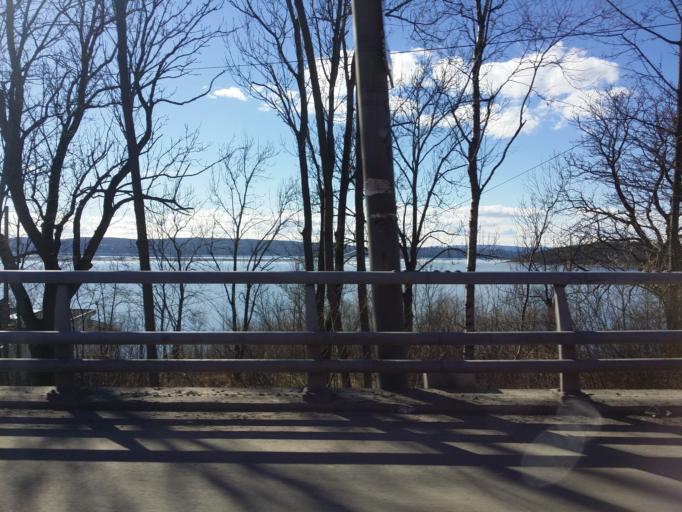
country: NO
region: Akershus
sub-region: Oppegard
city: Kolbotn
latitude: 59.8613
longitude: 10.7851
